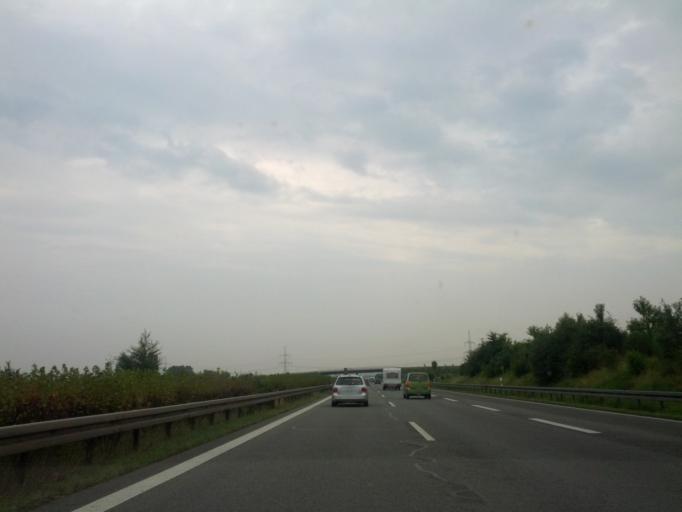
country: DE
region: Mecklenburg-Vorpommern
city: Papendorf
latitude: 54.0202
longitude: 12.0899
